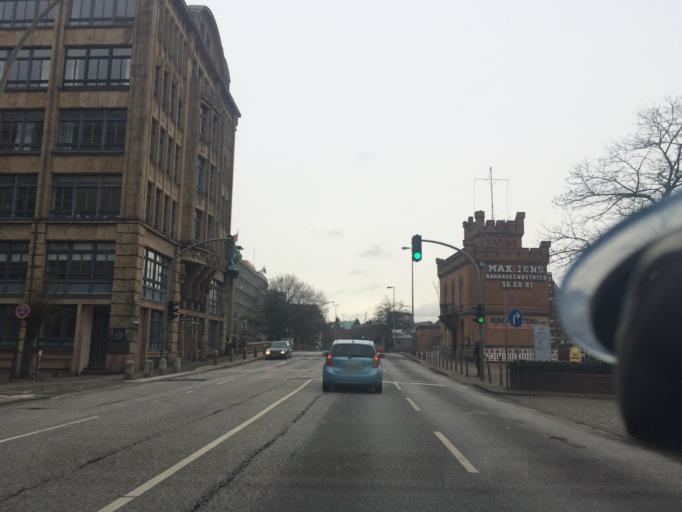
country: DE
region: Hamburg
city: Neustadt
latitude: 53.5450
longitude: 9.9862
